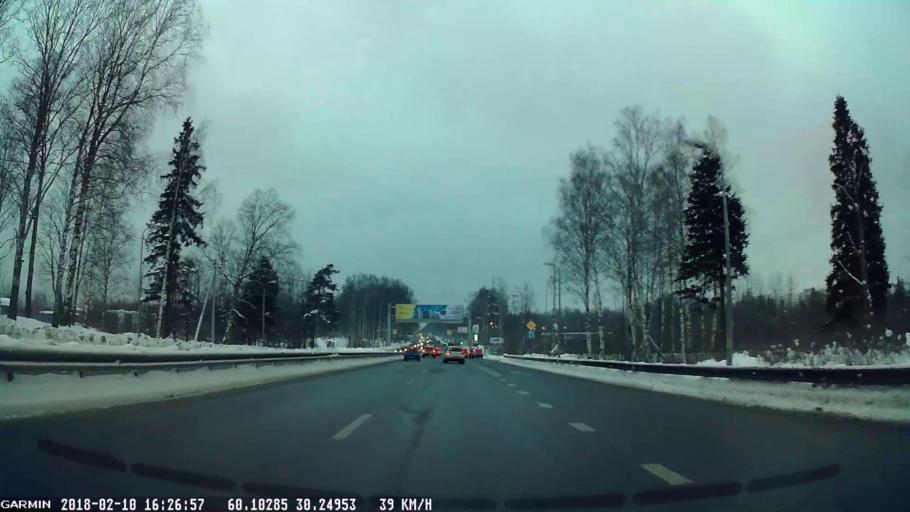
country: RU
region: St.-Petersburg
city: Pargolovo
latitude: 60.1029
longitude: 30.2495
